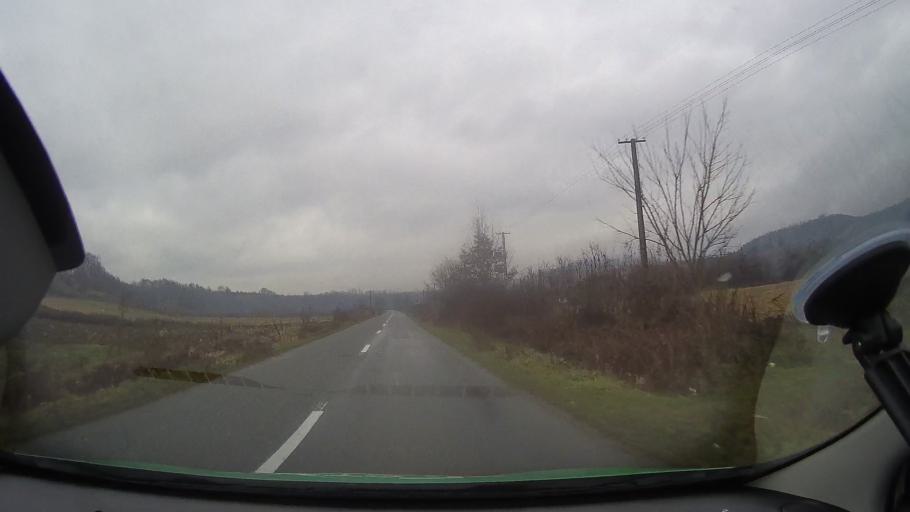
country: RO
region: Arad
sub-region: Comuna Brazii
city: Brazii
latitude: 46.2523
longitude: 22.3335
